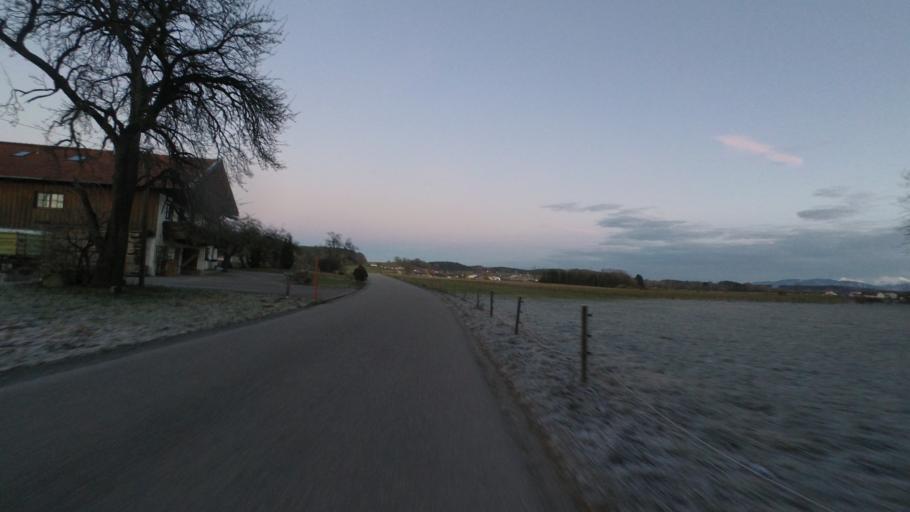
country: DE
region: Bavaria
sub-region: Upper Bavaria
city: Chieming
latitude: 47.9040
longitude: 12.5521
